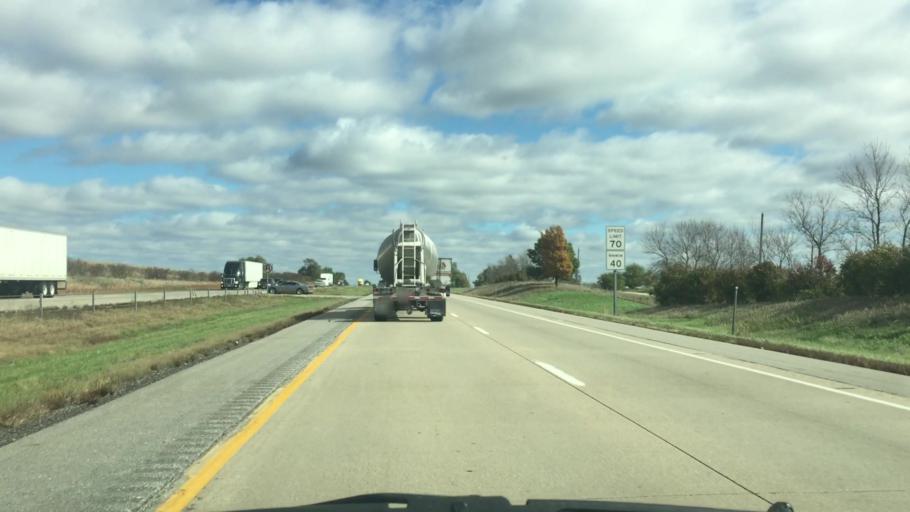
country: US
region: Iowa
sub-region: Poweshiek County
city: Brooklyn
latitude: 41.6960
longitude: -92.4329
